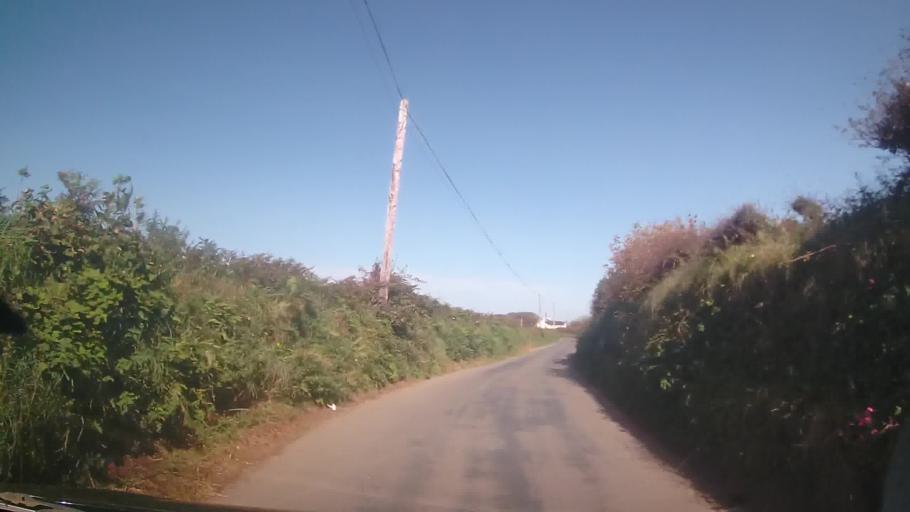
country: GB
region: Wales
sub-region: Pembrokeshire
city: Llanrhian
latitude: 51.9356
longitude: -5.1766
